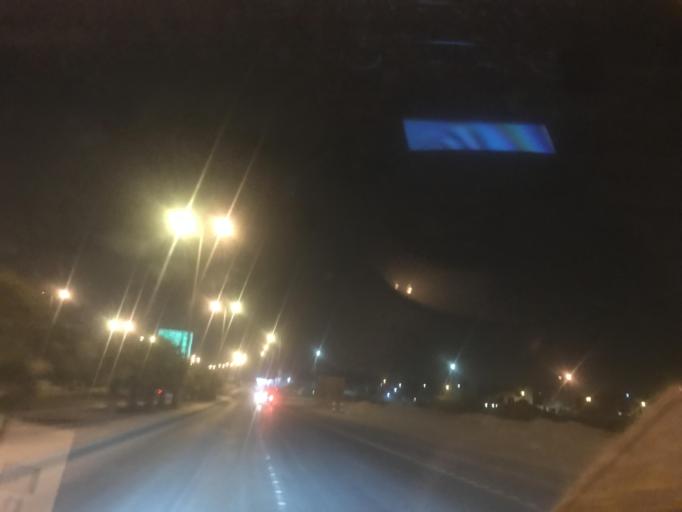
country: SA
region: Ar Riyad
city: Riyadh
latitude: 24.7875
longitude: 46.5900
